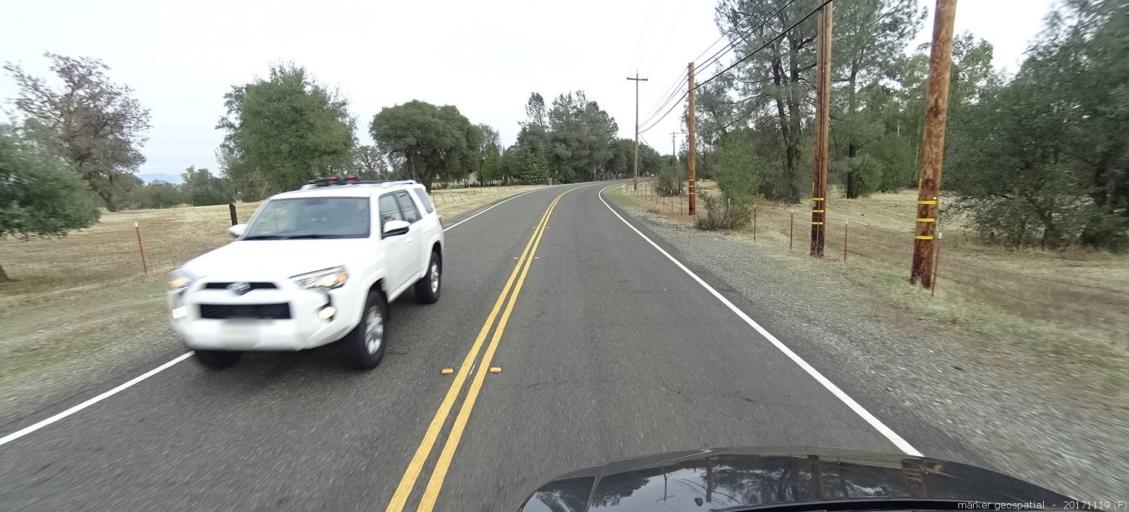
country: US
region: California
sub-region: Shasta County
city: Anderson
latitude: 40.4808
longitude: -122.3951
